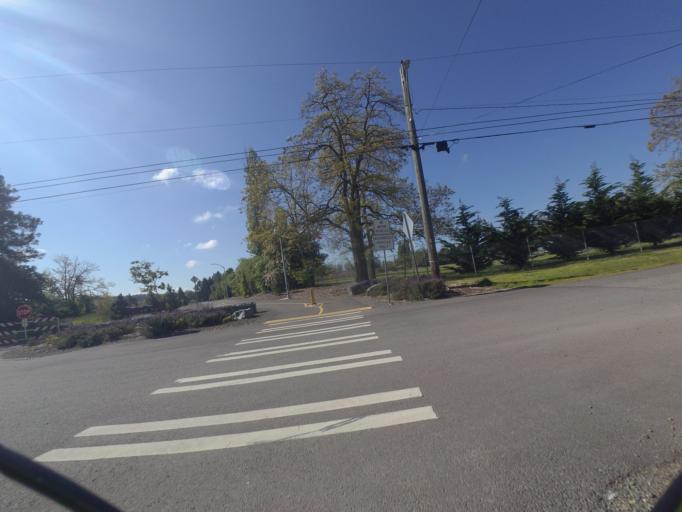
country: US
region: Washington
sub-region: Pierce County
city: Waller
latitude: 47.2155
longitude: -122.4124
